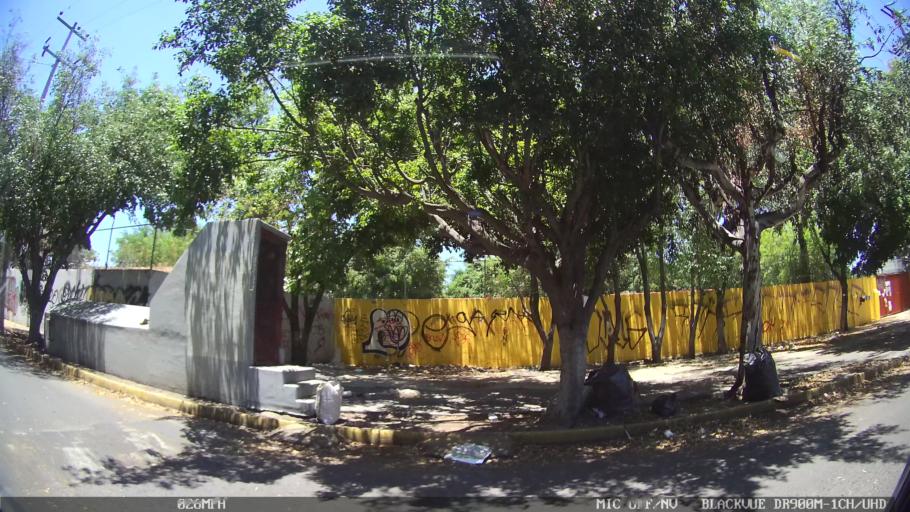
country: MX
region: Jalisco
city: Tlaquepaque
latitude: 20.6605
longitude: -103.2786
